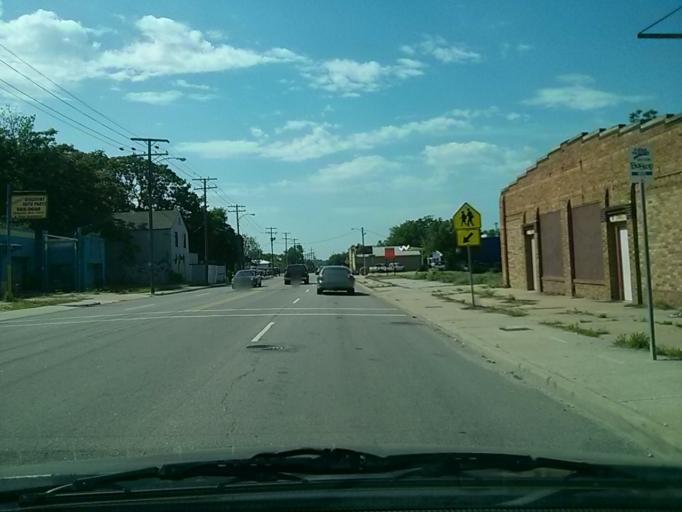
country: US
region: Oklahoma
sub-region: Tulsa County
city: Tulsa
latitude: 36.1659
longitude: -95.9756
